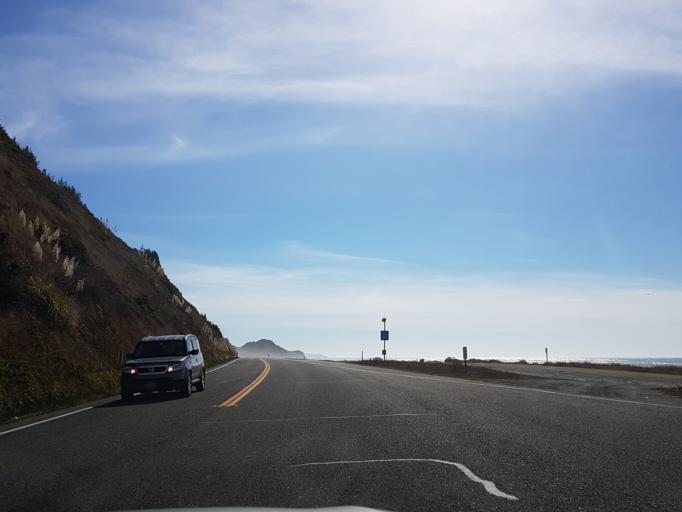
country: US
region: California
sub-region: Humboldt County
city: Westhaven-Moonstone
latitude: 41.2816
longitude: -124.0930
